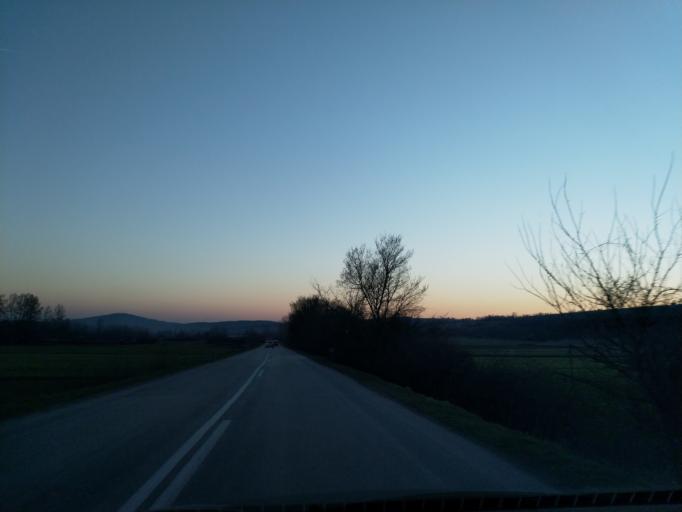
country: RS
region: Central Serbia
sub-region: Pomoravski Okrug
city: Paracin
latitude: 43.8975
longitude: 21.4905
